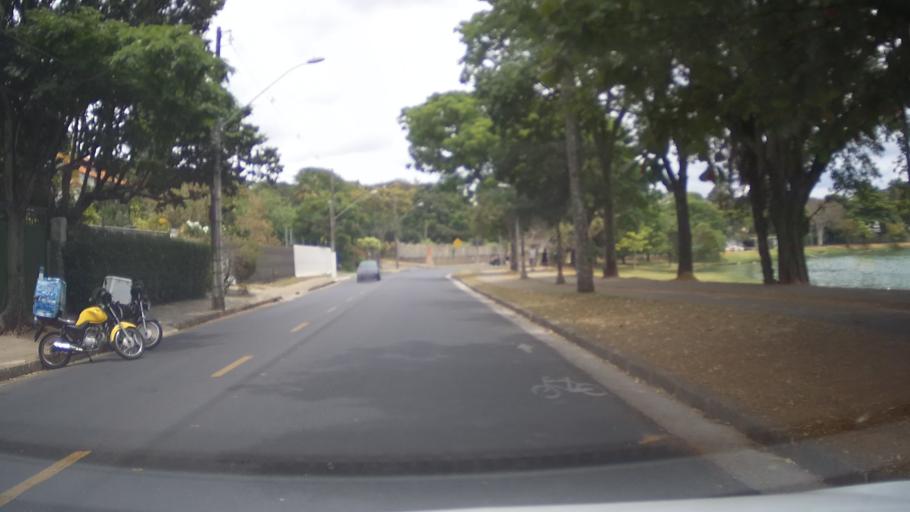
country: BR
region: Minas Gerais
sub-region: Belo Horizonte
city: Belo Horizonte
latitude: -19.8523
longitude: -43.9884
